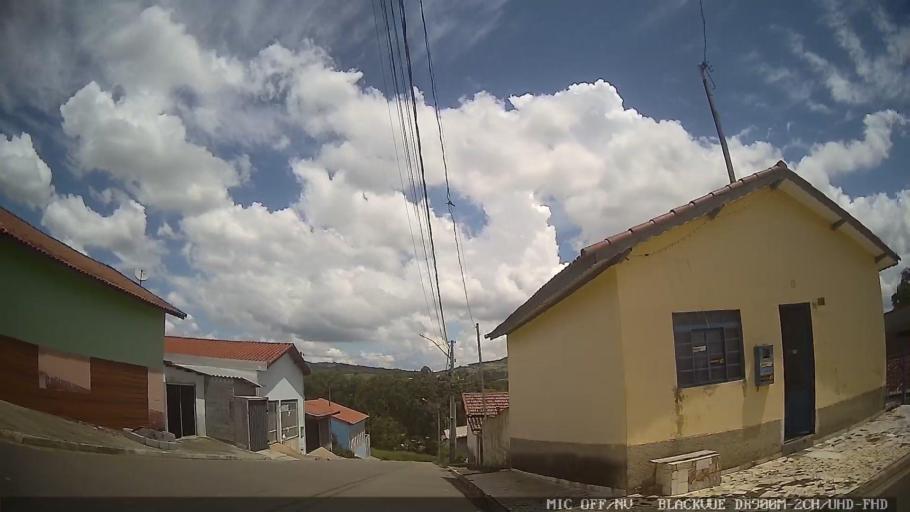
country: BR
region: Minas Gerais
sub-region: Extrema
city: Extrema
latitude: -22.7421
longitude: -46.3784
